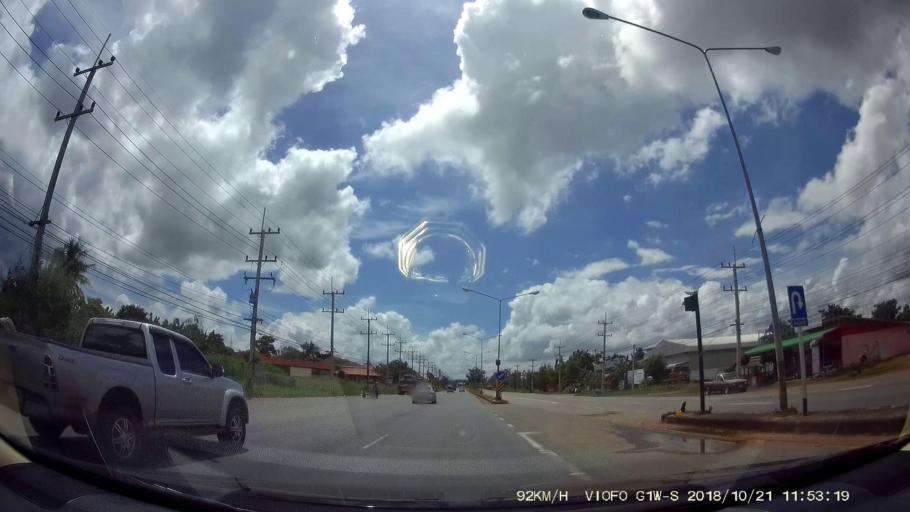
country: TH
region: Chaiyaphum
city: Chatturat
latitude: 15.5973
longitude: 101.9067
